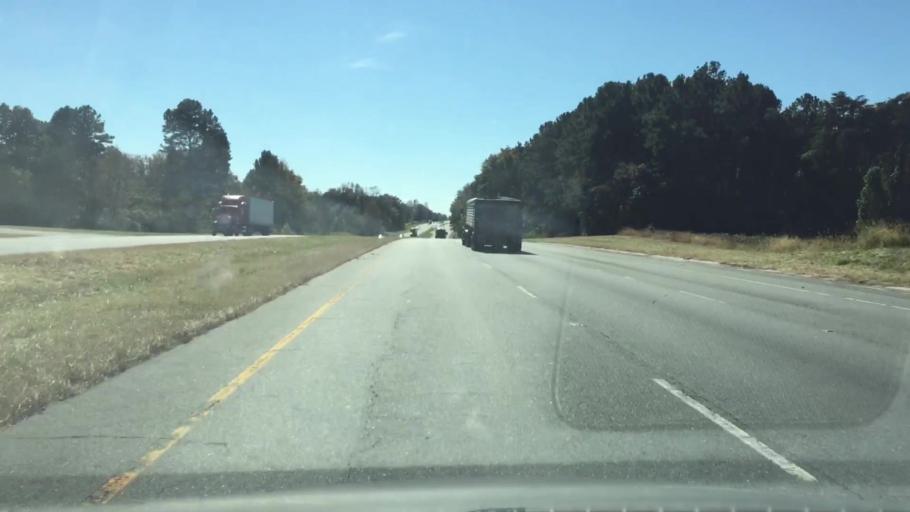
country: US
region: North Carolina
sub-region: Guilford County
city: McLeansville
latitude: 36.2258
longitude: -79.6795
